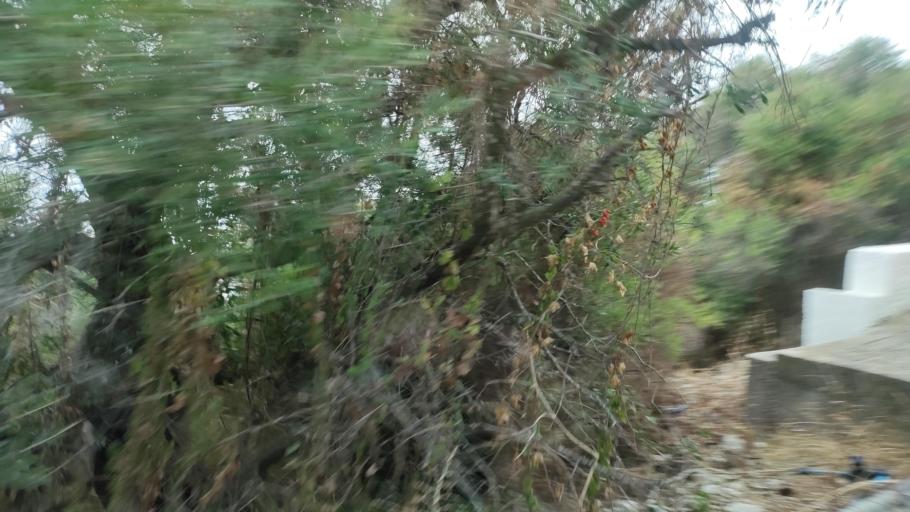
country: GI
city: Gibraltar
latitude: 36.1371
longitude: -5.3492
